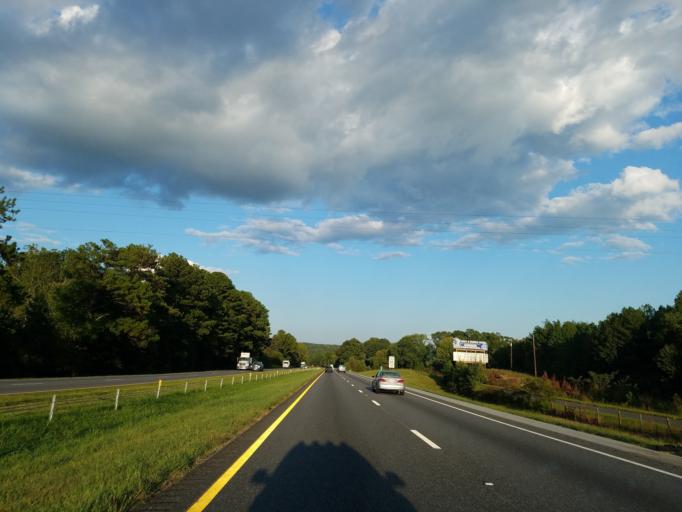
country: US
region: South Carolina
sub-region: Cherokee County
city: East Gaffney
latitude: 35.1102
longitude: -81.5951
